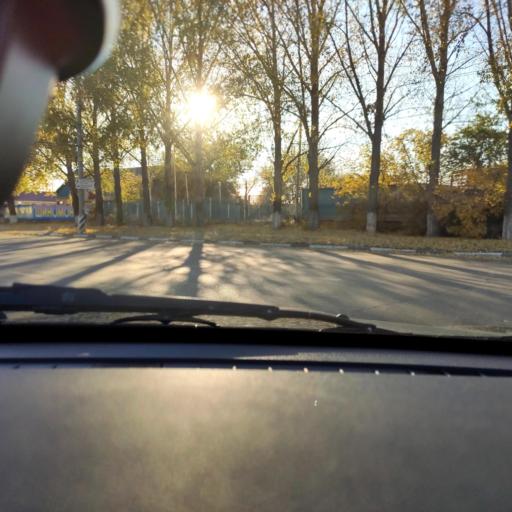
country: RU
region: Samara
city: Tol'yatti
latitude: 53.5230
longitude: 49.2594
